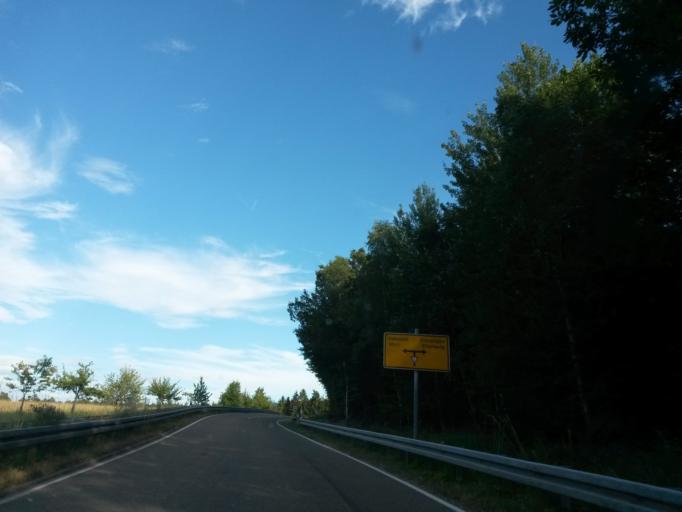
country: DE
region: Baden-Wuerttemberg
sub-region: Regierungsbezirk Stuttgart
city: Wort
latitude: 49.0376
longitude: 10.2411
